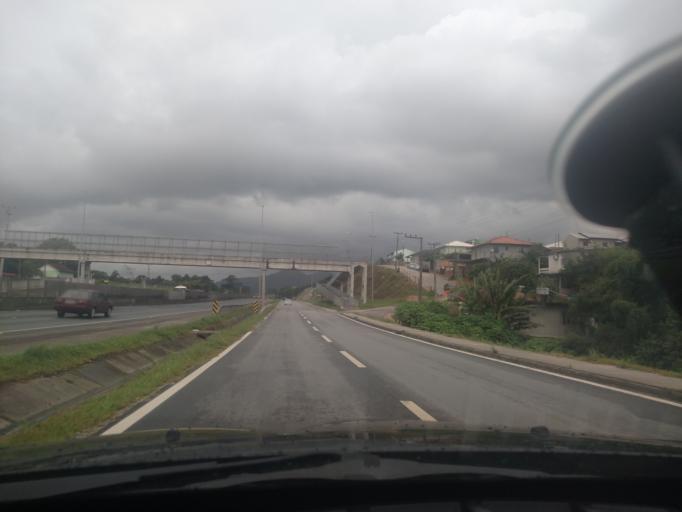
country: BR
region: Santa Catarina
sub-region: Biguacu
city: Biguacu
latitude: -27.3832
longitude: -48.6313
